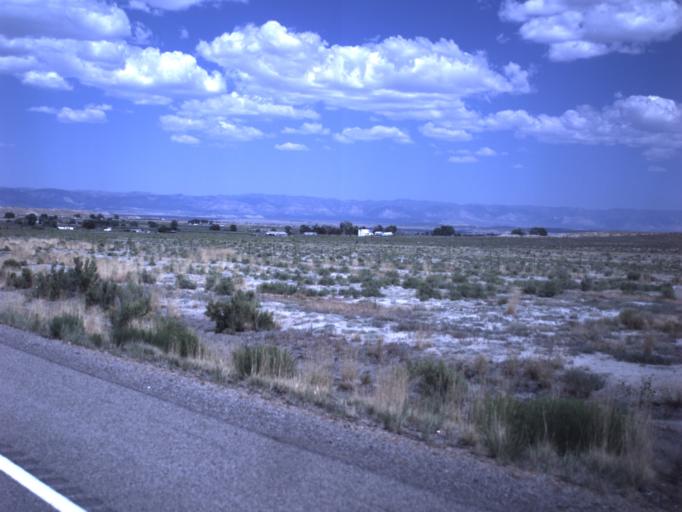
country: US
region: Utah
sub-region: Carbon County
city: Price
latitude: 39.5100
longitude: -110.8337
